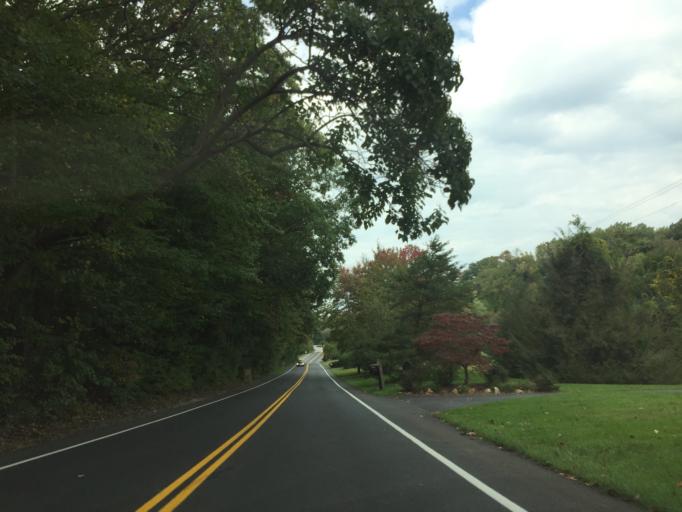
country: US
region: Maryland
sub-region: Harford County
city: Bel Air South
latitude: 39.4918
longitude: -76.3128
